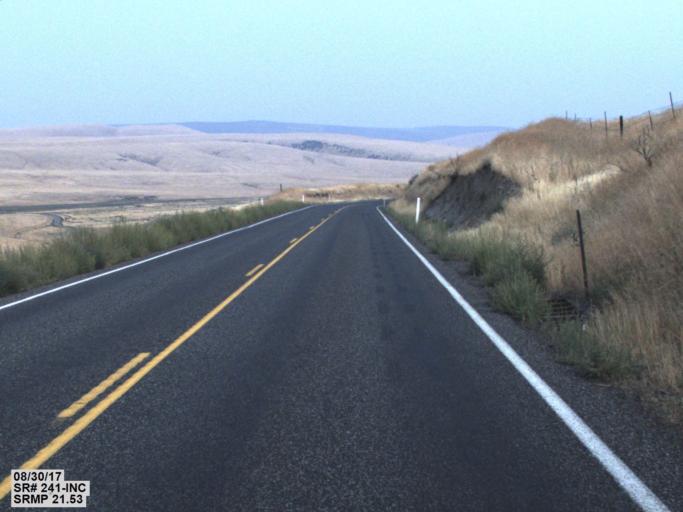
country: US
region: Washington
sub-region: Grant County
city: Desert Aire
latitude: 46.4931
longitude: -119.9064
